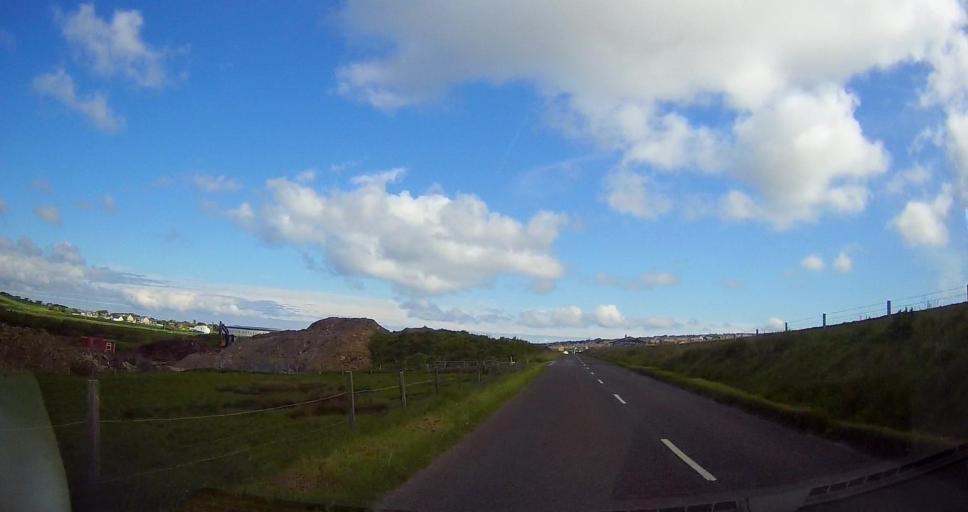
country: GB
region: Scotland
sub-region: Orkney Islands
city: Orkney
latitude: 58.9676
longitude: -2.9642
